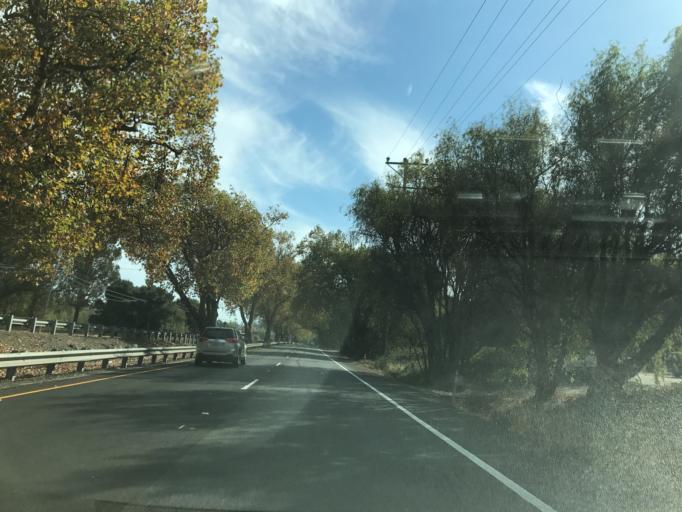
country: US
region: California
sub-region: Sonoma County
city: Penngrove
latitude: 38.2665
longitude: -122.6706
